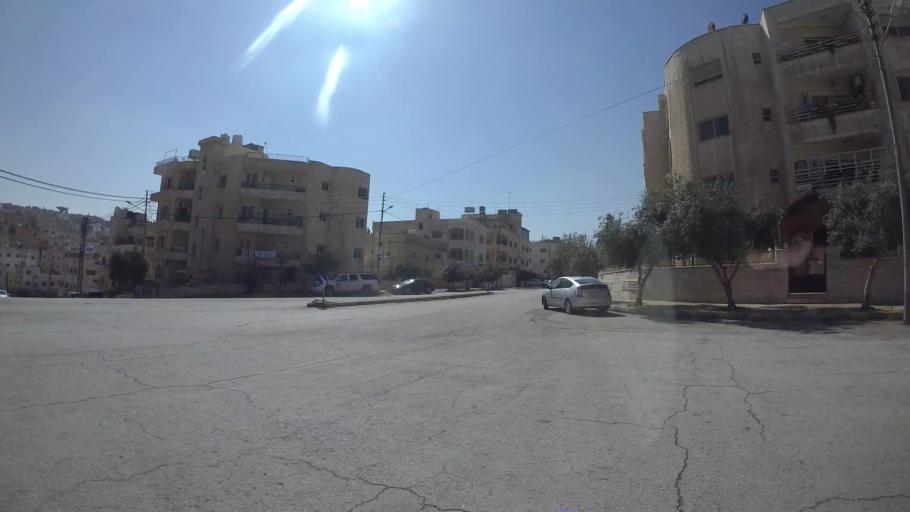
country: JO
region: Amman
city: Amman
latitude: 31.9874
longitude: 35.9818
